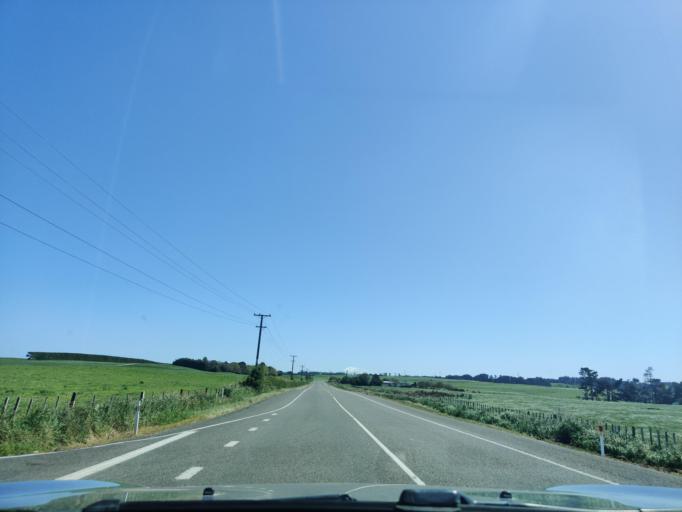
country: NZ
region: Taranaki
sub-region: South Taranaki District
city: Patea
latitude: -39.7830
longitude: 174.6960
